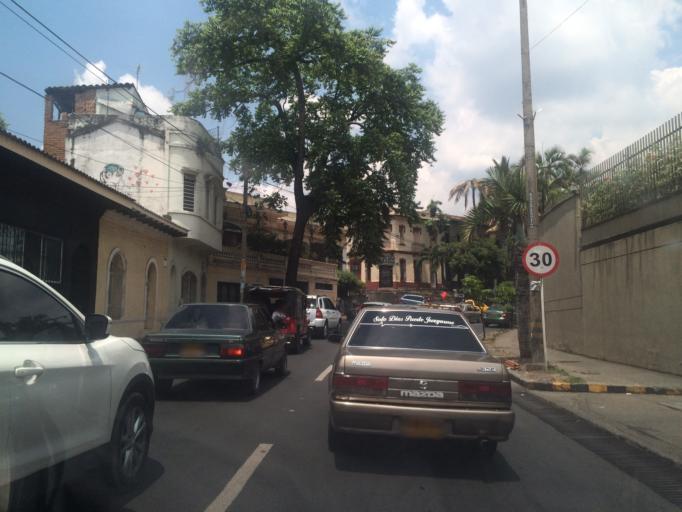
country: CO
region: Valle del Cauca
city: Cali
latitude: 3.4493
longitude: -76.5384
